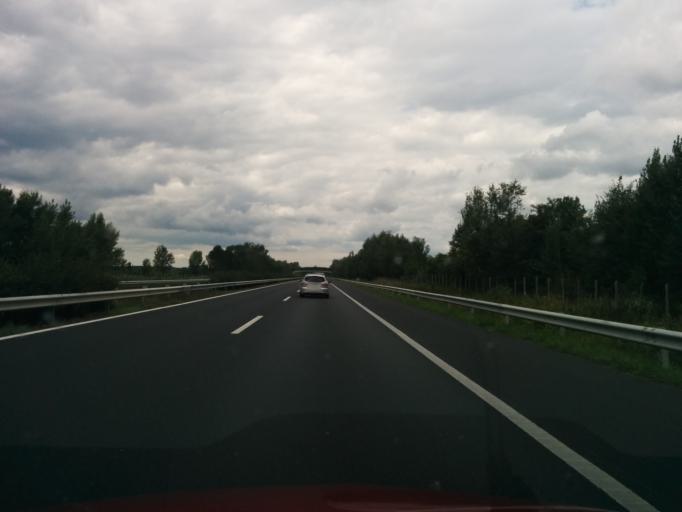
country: HU
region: Gyor-Moson-Sopron
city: Kimle
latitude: 47.7753
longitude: 17.3628
